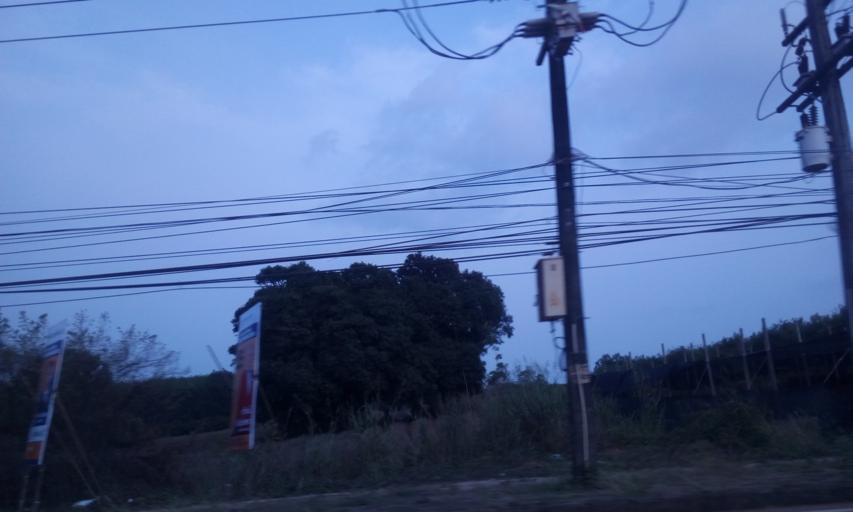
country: TH
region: Trat
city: Khao Saming
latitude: 12.3649
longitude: 102.3854
